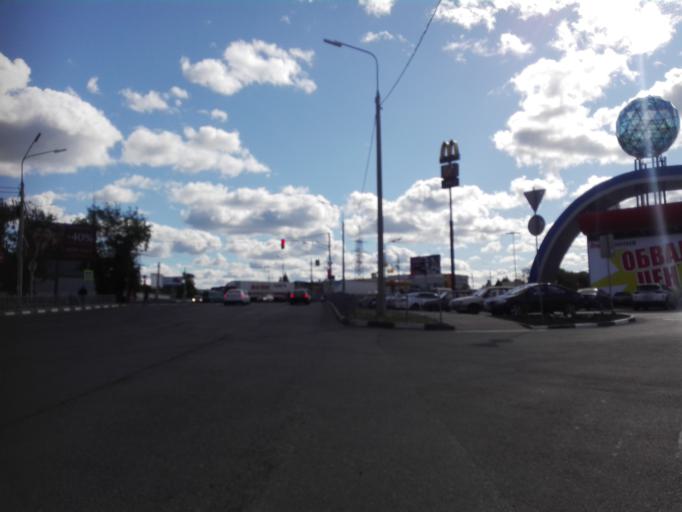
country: RU
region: Orjol
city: Orel
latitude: 52.9472
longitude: 36.0338
